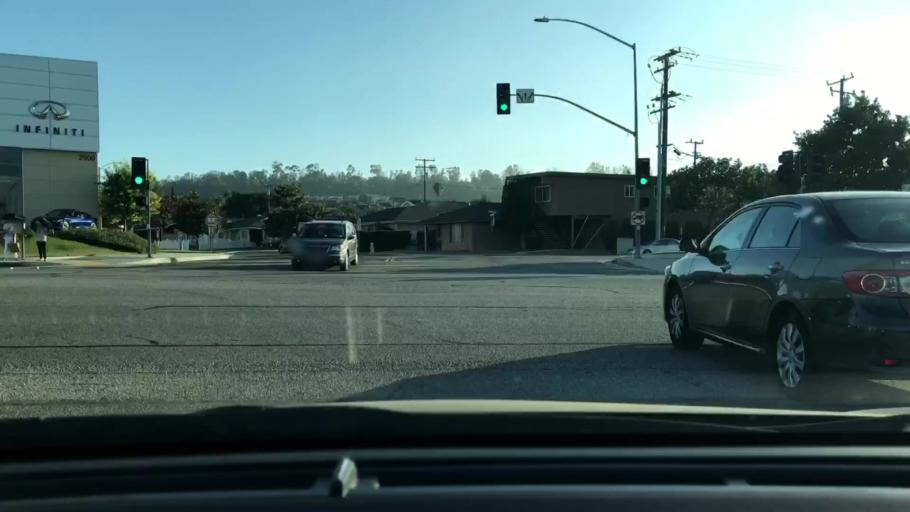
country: US
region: California
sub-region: Los Angeles County
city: Rolling Hills Estates
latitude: 33.7960
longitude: -118.3382
